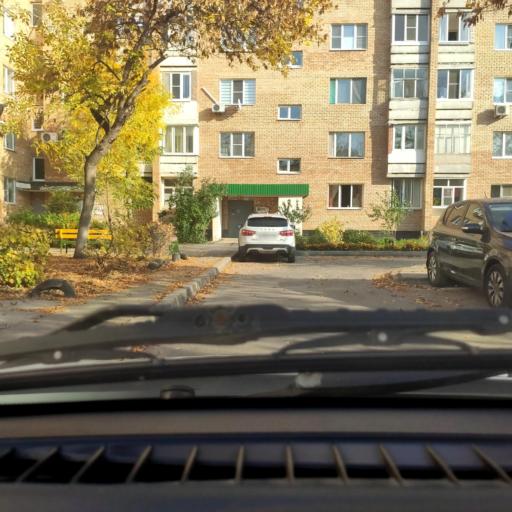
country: RU
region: Samara
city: Tol'yatti
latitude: 53.5173
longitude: 49.2969
